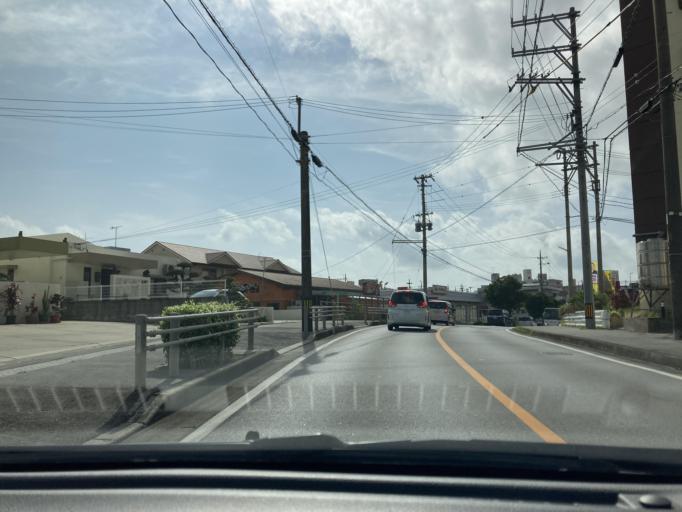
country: JP
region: Okinawa
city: Ginowan
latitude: 26.2581
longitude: 127.7684
